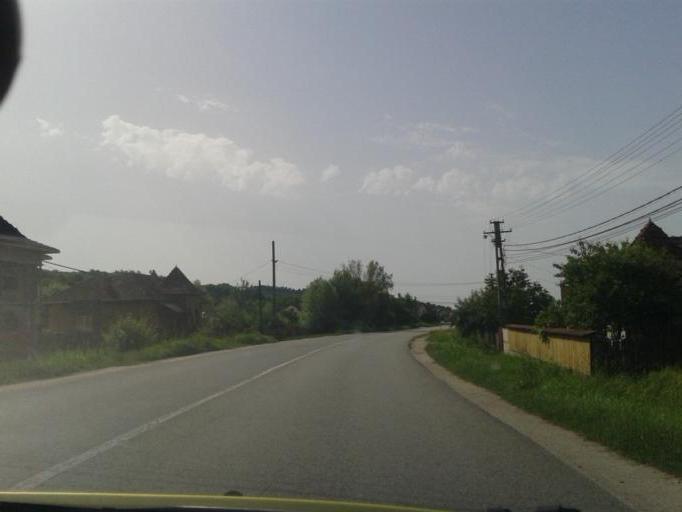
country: RO
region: Valcea
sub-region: Comuna Mihaesti
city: Mihaesti
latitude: 45.0608
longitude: 24.2462
